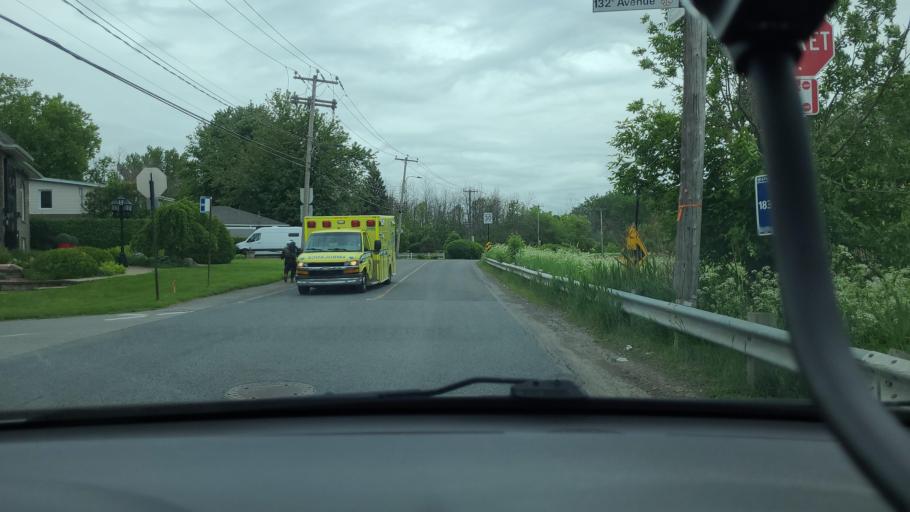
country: CA
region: Quebec
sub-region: Lanaudiere
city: Charlemagne
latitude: 45.6968
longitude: -73.5001
